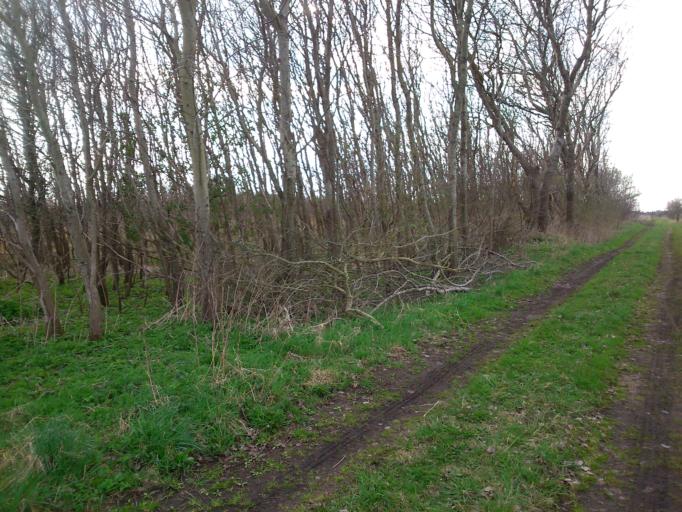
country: DK
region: South Denmark
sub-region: Tonder Kommune
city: Tonder
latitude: 55.0254
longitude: 8.8438
